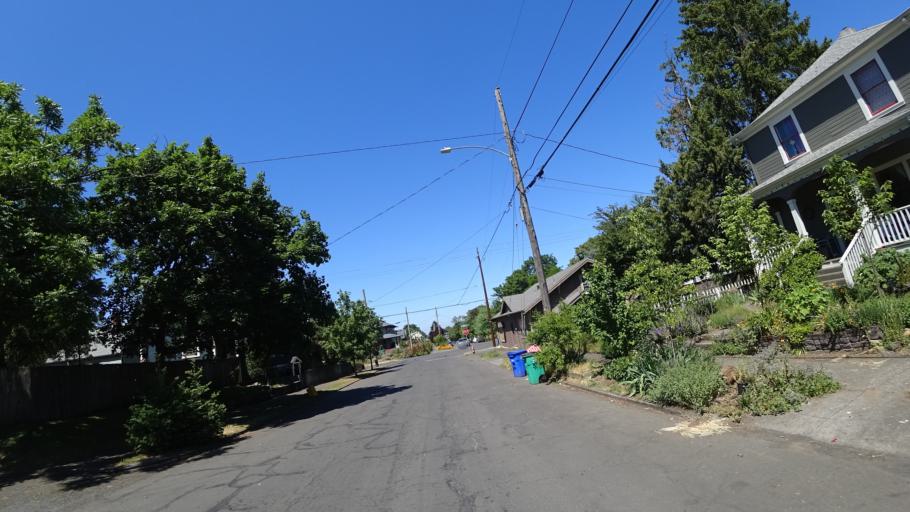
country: US
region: Oregon
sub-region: Multnomah County
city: Portland
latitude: 45.5658
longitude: -122.6561
